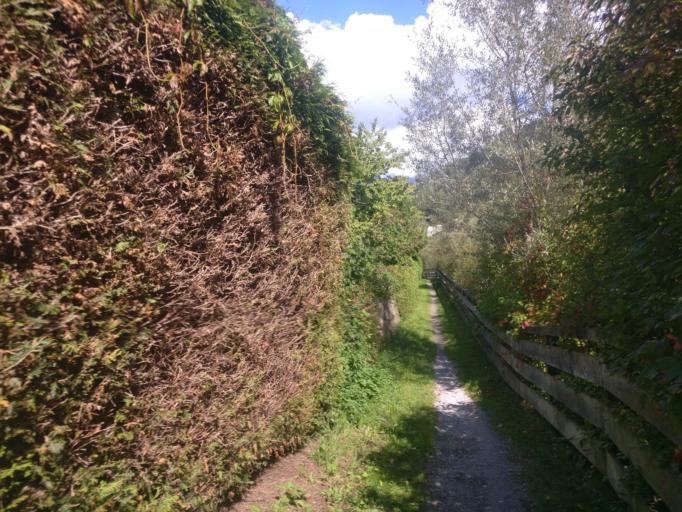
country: AT
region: Salzburg
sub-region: Politischer Bezirk Sankt Johann im Pongau
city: Bischofshofen
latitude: 47.4112
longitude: 13.2198
